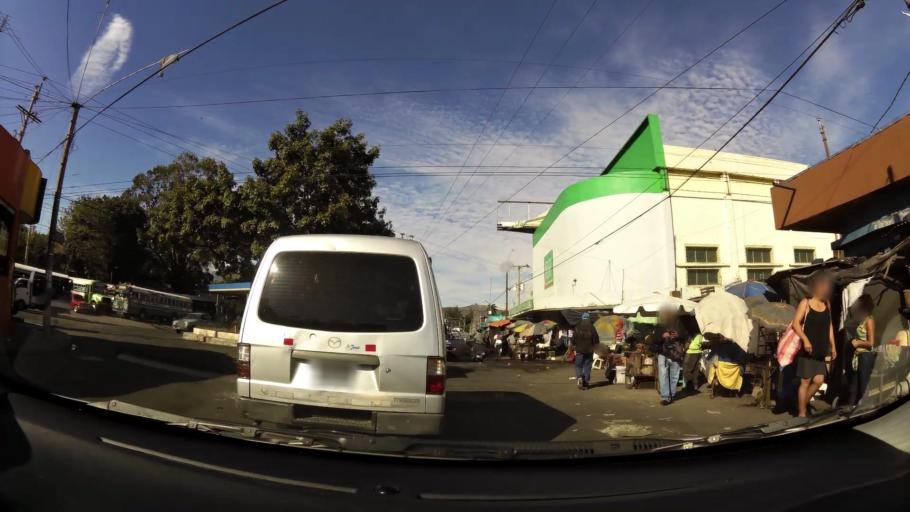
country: SV
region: Santa Ana
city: Santa Ana
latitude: 13.9884
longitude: -89.5653
